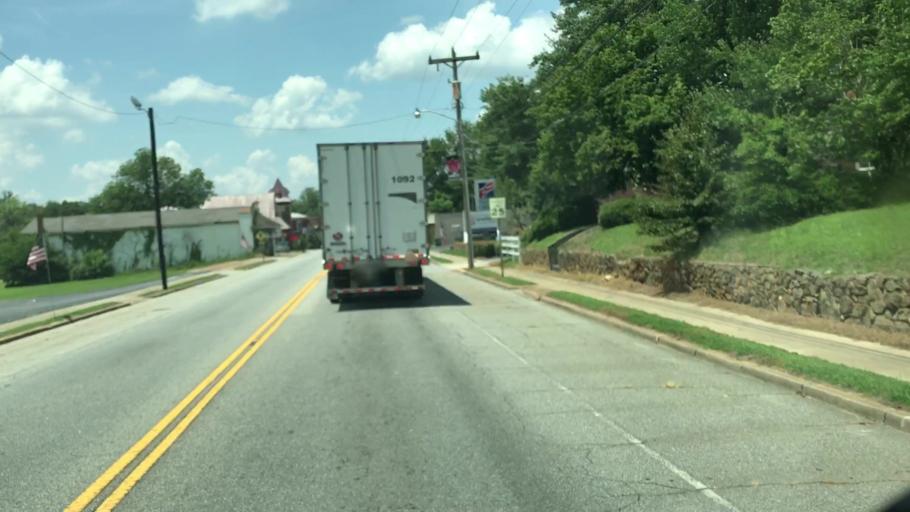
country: US
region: South Carolina
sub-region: Anderson County
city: Williamston
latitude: 34.6198
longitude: -82.4746
